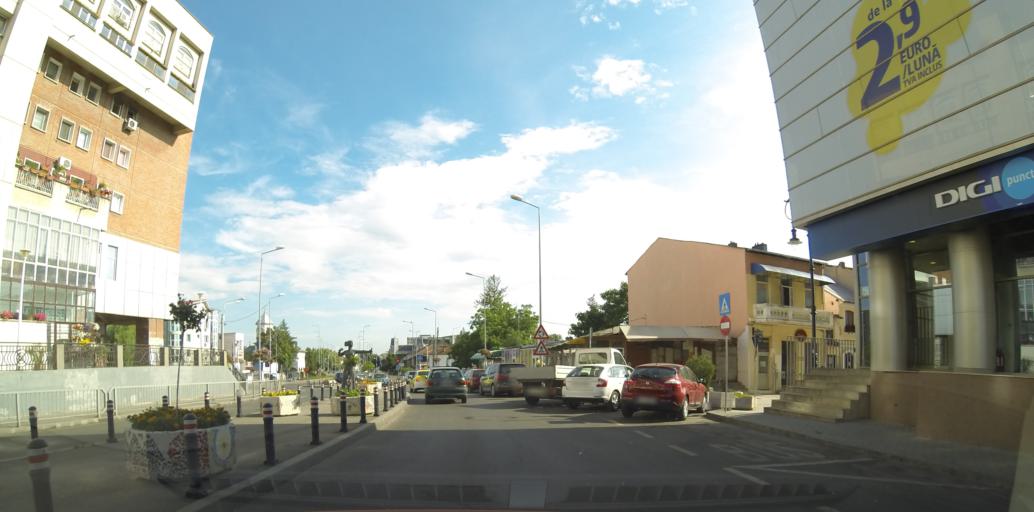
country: RO
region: Dolj
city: Craiova
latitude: 44.3175
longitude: 23.8012
